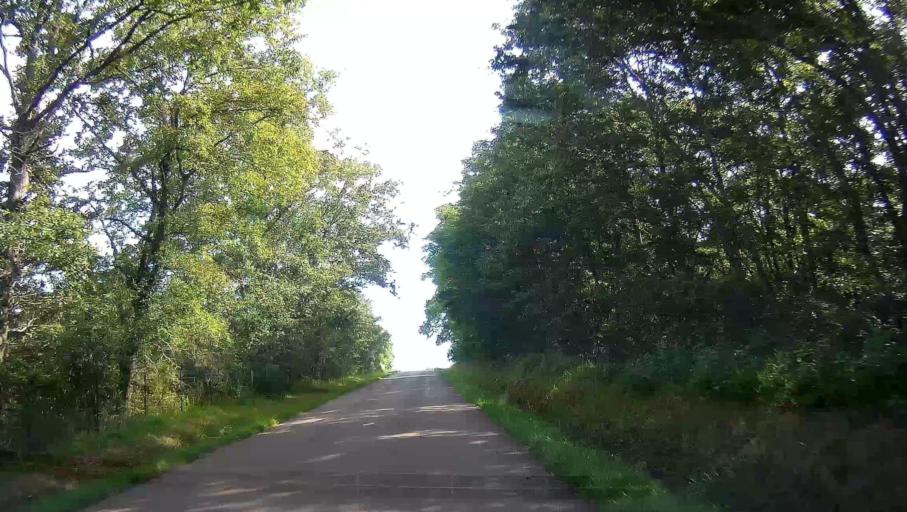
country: FR
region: Bourgogne
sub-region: Departement de Saone-et-Loire
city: Saint-Leger-sur-Dheune
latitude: 46.8722
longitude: 4.6317
